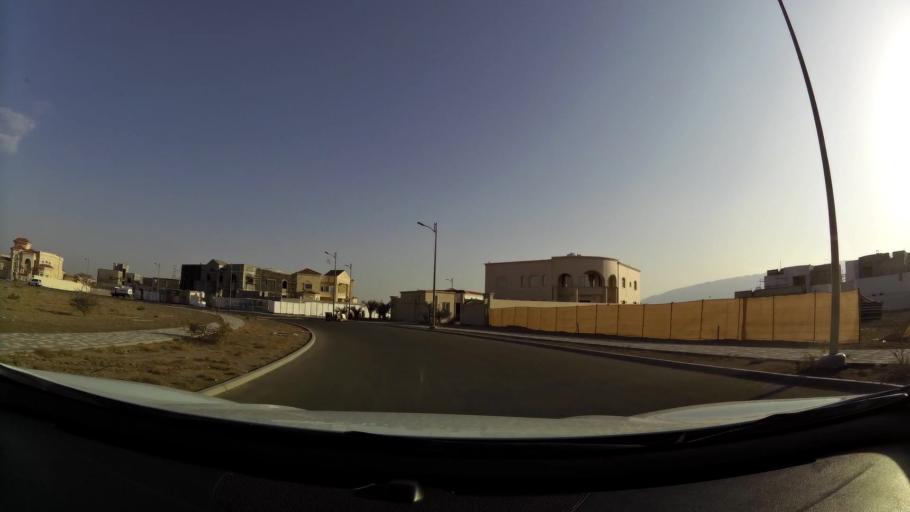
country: AE
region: Abu Dhabi
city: Al Ain
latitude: 24.1048
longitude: 55.8494
